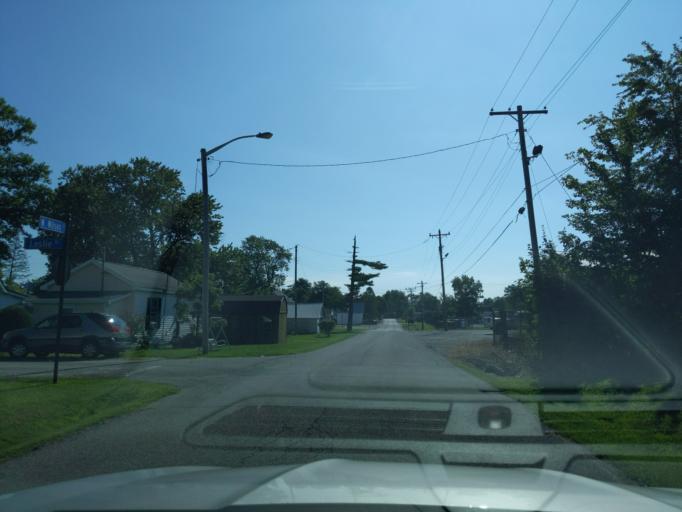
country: US
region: Indiana
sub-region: Ripley County
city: Osgood
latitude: 39.1246
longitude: -85.2925
